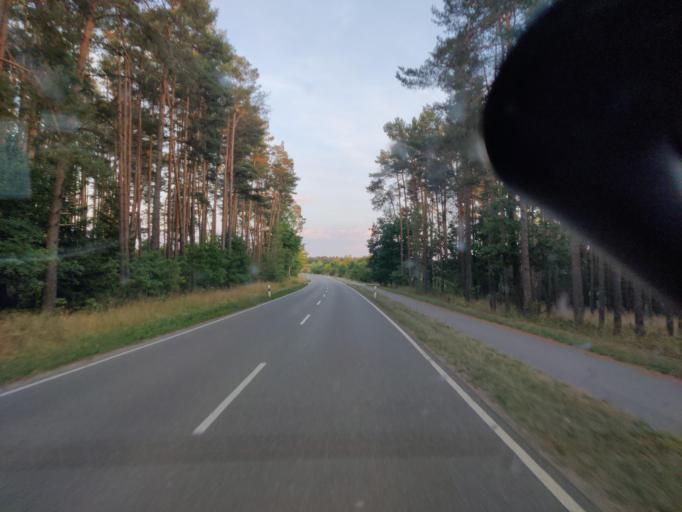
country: DE
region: Bavaria
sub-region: Regierungsbezirk Mittelfranken
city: Hilpoltstein
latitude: 49.1652
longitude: 11.1909
